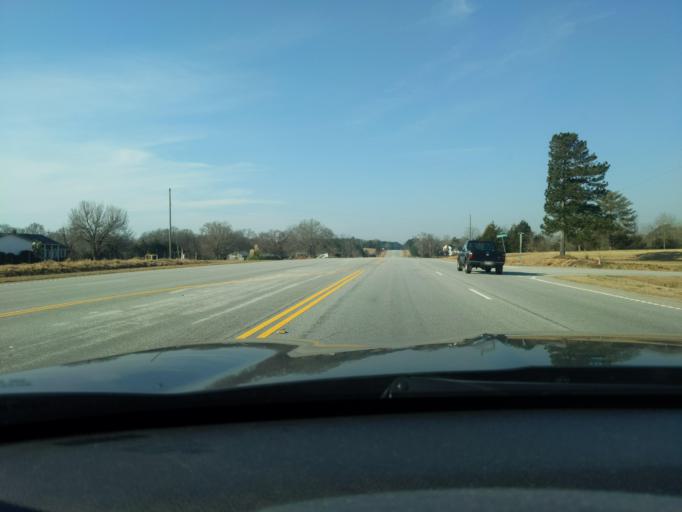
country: US
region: South Carolina
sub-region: Abbeville County
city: Abbeville
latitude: 34.1276
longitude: -82.4334
